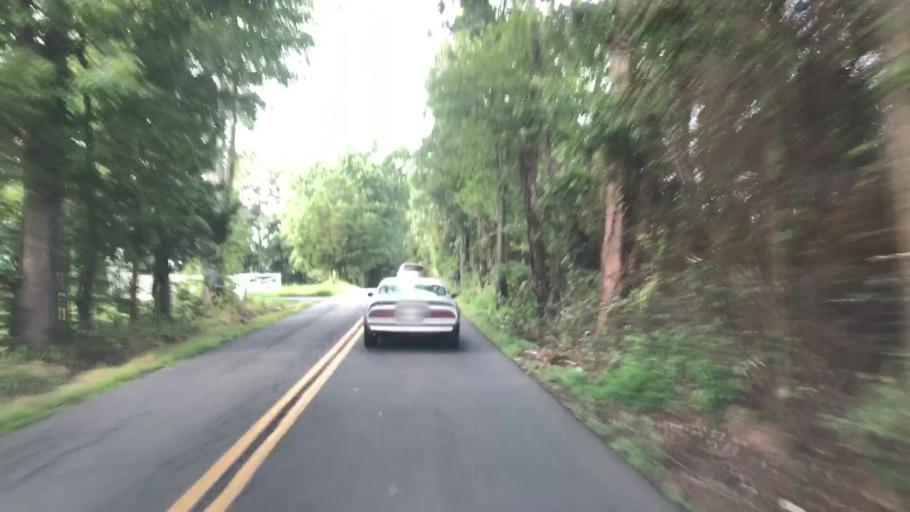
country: US
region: Virginia
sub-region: Prince William County
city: Gainesville
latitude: 38.7423
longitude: -77.6516
